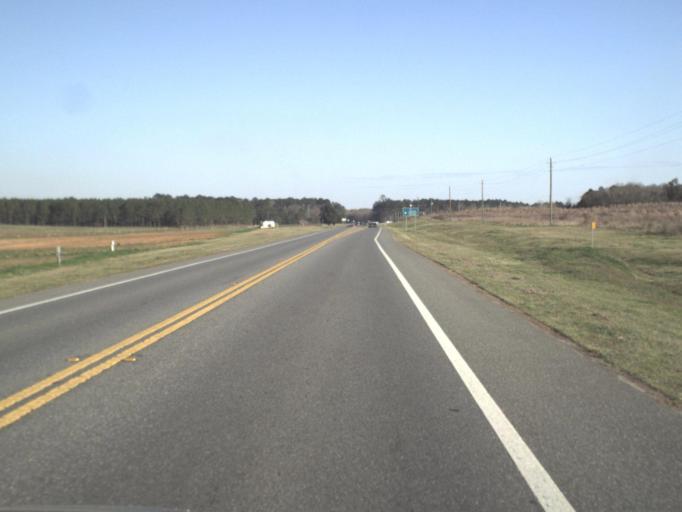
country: US
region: Florida
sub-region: Jackson County
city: Sneads
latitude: 30.7032
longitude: -84.8840
